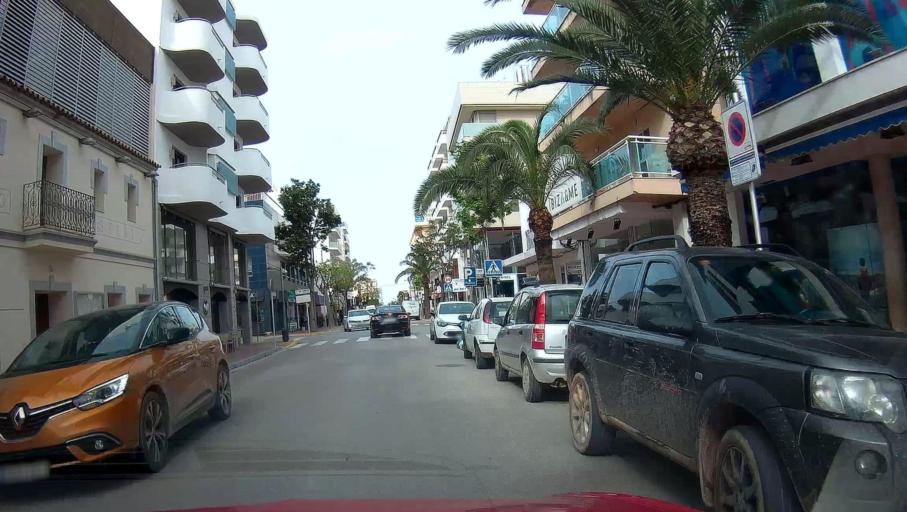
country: ES
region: Balearic Islands
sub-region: Illes Balears
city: Santa Eularia des Riu
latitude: 38.9857
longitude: 1.5358
